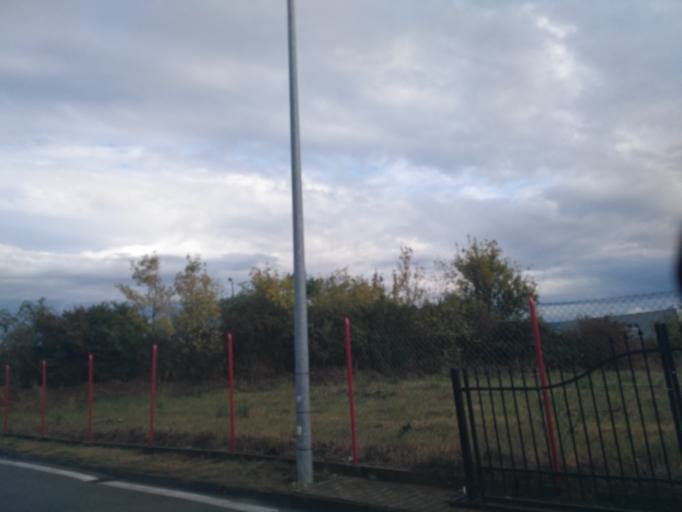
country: SK
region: Kosicky
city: Kosice
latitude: 48.6945
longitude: 21.2443
